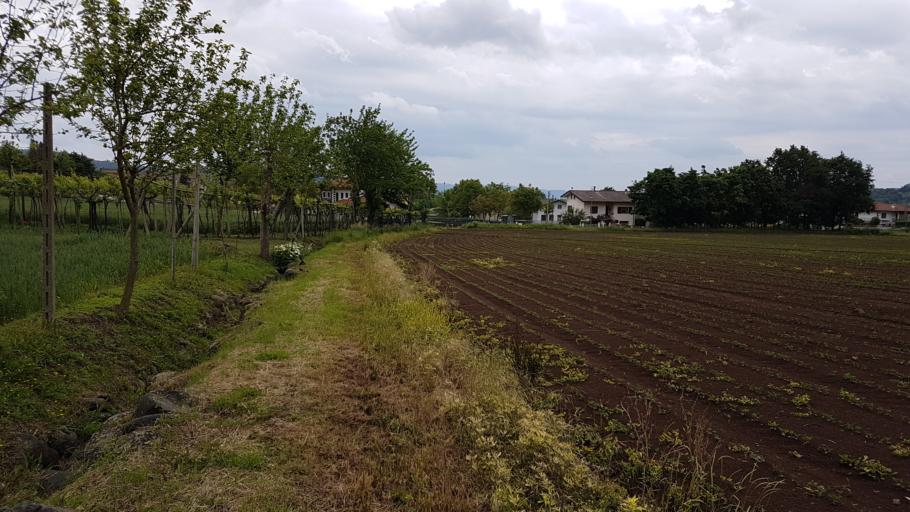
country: IT
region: Veneto
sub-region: Provincia di Vicenza
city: Tezze
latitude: 45.5474
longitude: 11.3423
